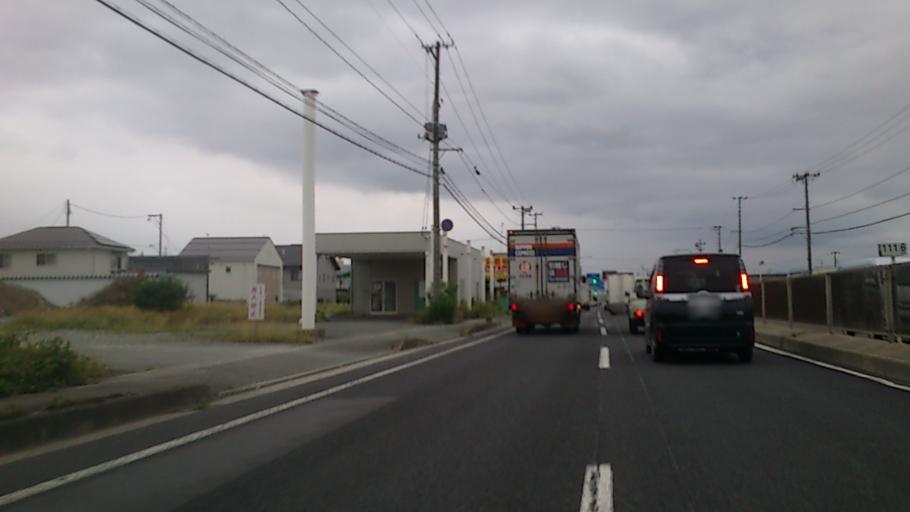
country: JP
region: Yamagata
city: Higashine
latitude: 38.4312
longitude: 140.3776
